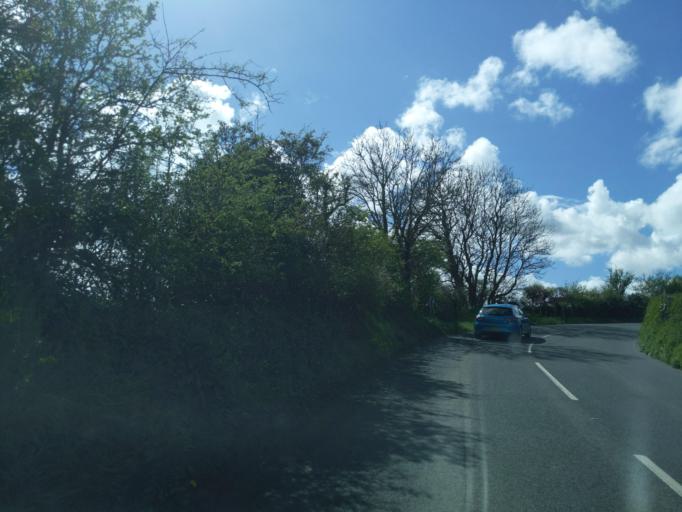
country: GB
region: England
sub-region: Cornwall
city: Wadebridge
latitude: 50.5417
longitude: -4.8593
